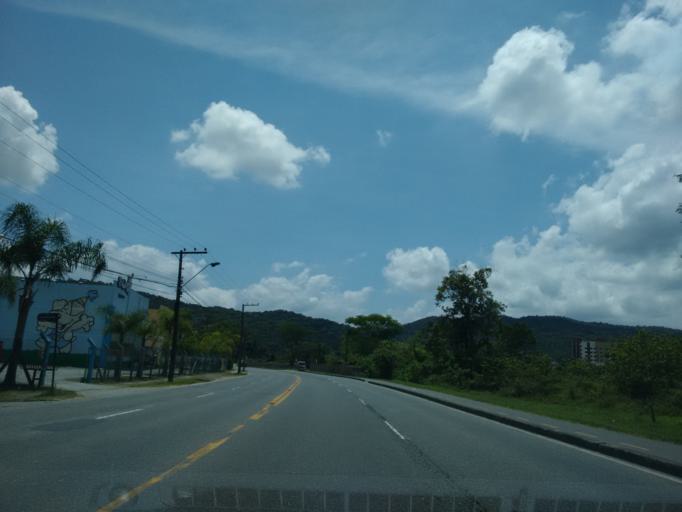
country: BR
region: Santa Catarina
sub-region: Blumenau
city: Blumenau
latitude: -26.9062
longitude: -49.0451
